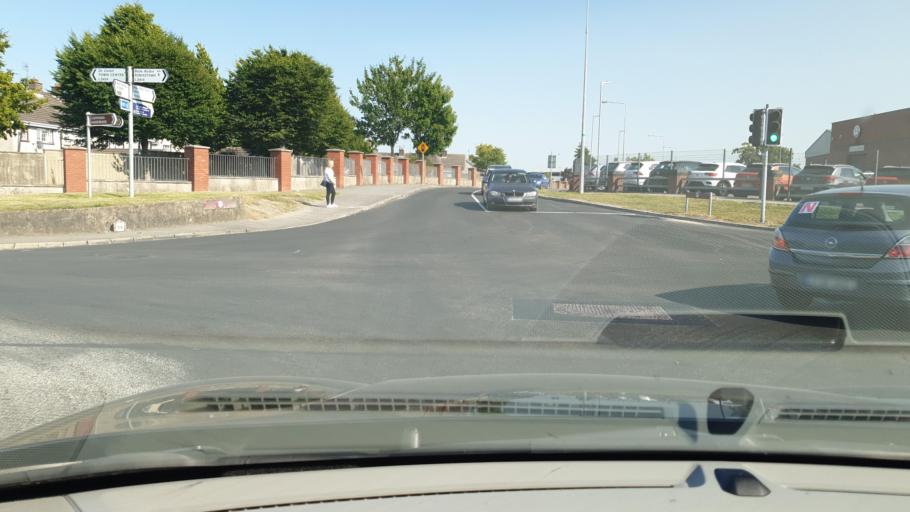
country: IE
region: Leinster
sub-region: An Mhi
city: Navan
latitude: 53.6465
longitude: -6.6986
